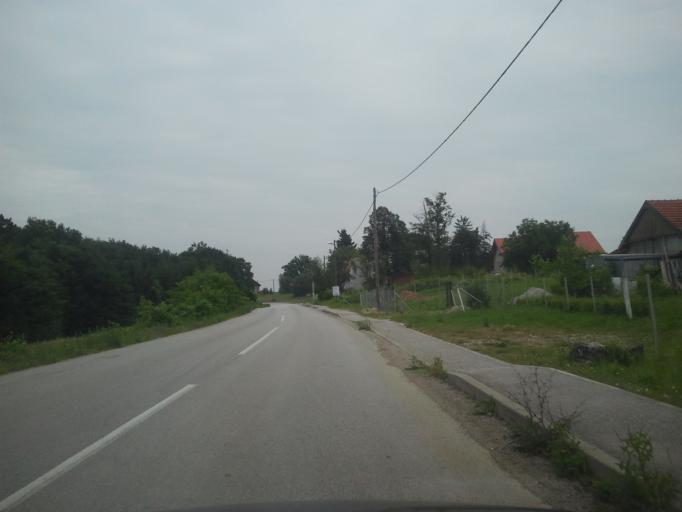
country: HR
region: Grad Zagreb
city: Strmec
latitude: 45.6230
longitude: 15.8668
